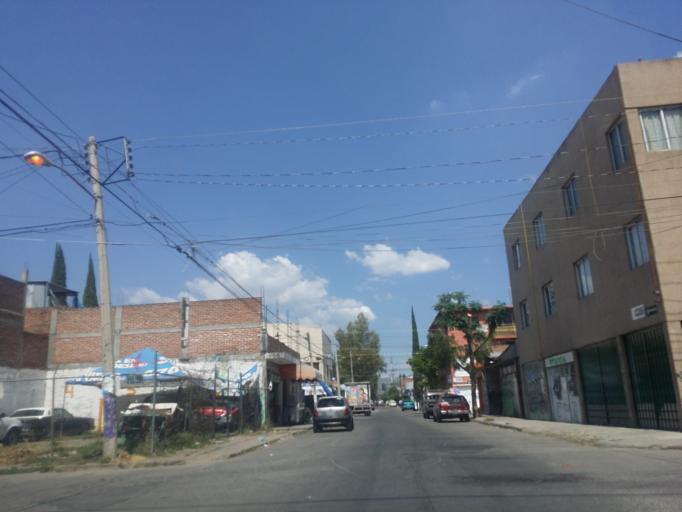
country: MX
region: Guanajuato
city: Leon
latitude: 21.1440
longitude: -101.6665
